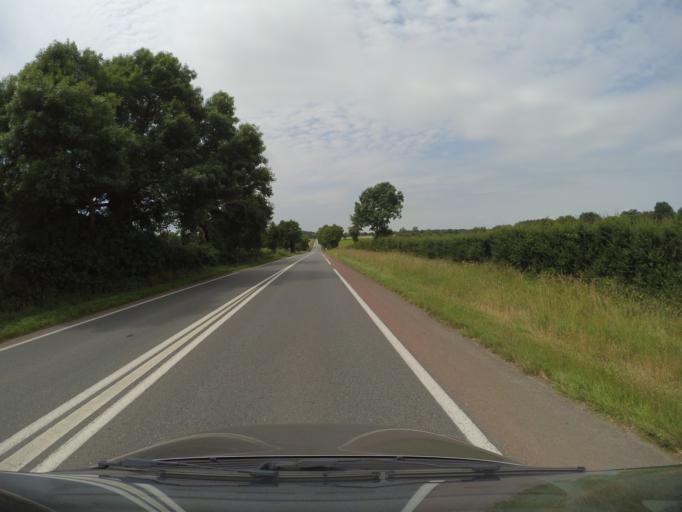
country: FR
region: Pays de la Loire
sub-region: Departement de la Vendee
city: Vendrennes
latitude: 46.8434
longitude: -1.0776
